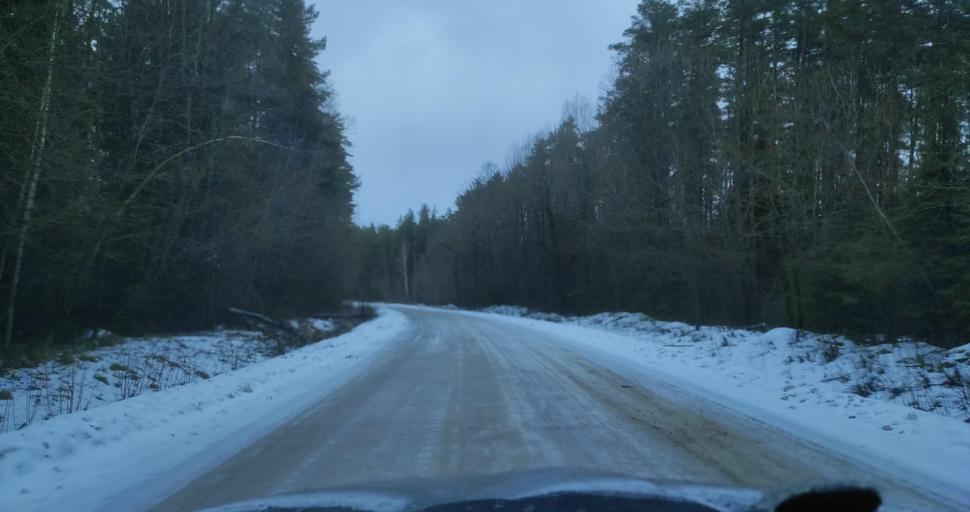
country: LV
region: Dundaga
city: Dundaga
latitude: 57.4904
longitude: 22.0190
